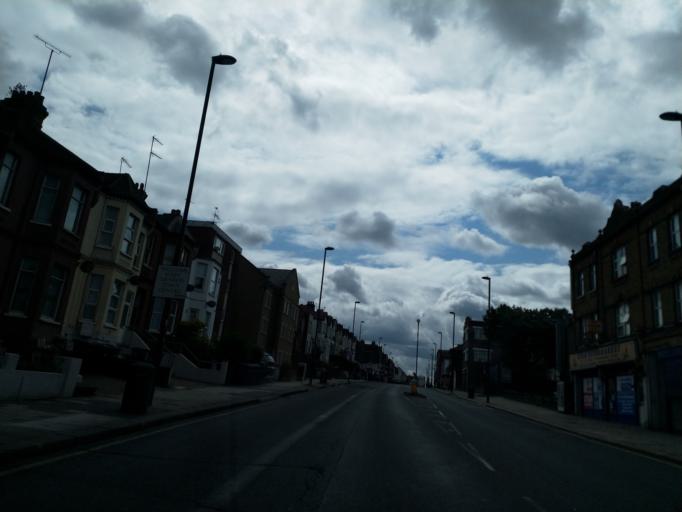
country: GB
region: England
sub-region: Greater London
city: Hendon
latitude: 51.5800
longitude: -0.2424
